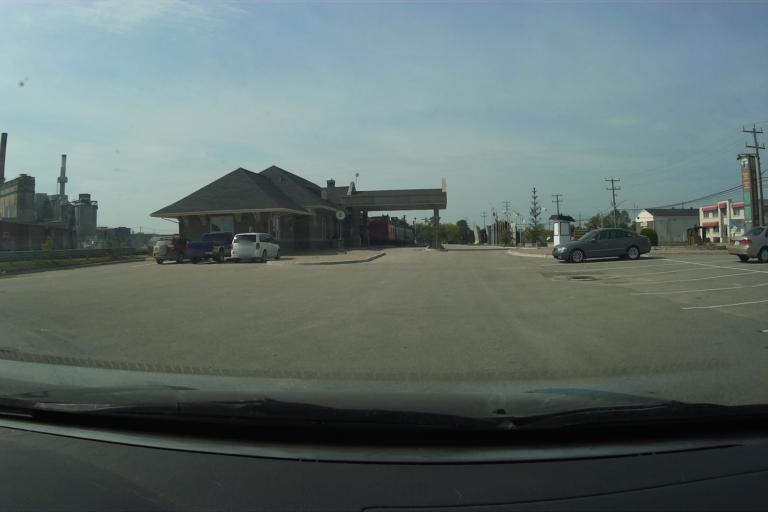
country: CA
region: Ontario
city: Kapuskasing
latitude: 49.4126
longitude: -82.4229
